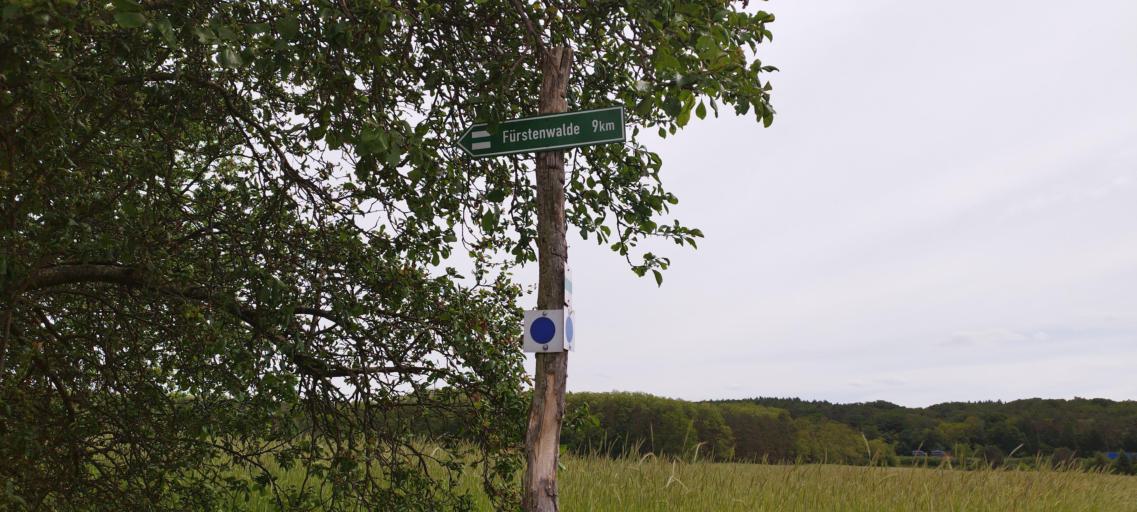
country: DE
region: Brandenburg
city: Rauen
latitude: 52.3323
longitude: 14.0337
